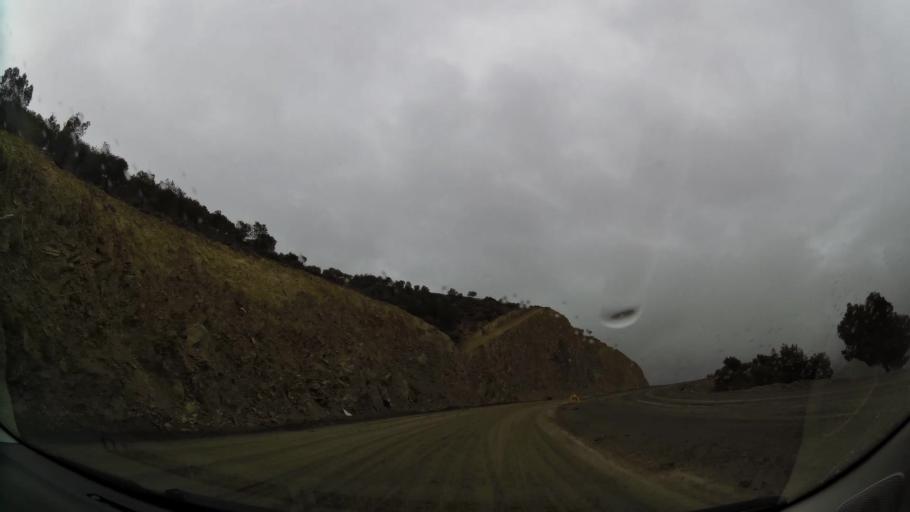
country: MA
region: Taza-Al Hoceima-Taounate
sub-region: Taza
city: Ajdir
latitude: 34.8996
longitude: -3.7846
